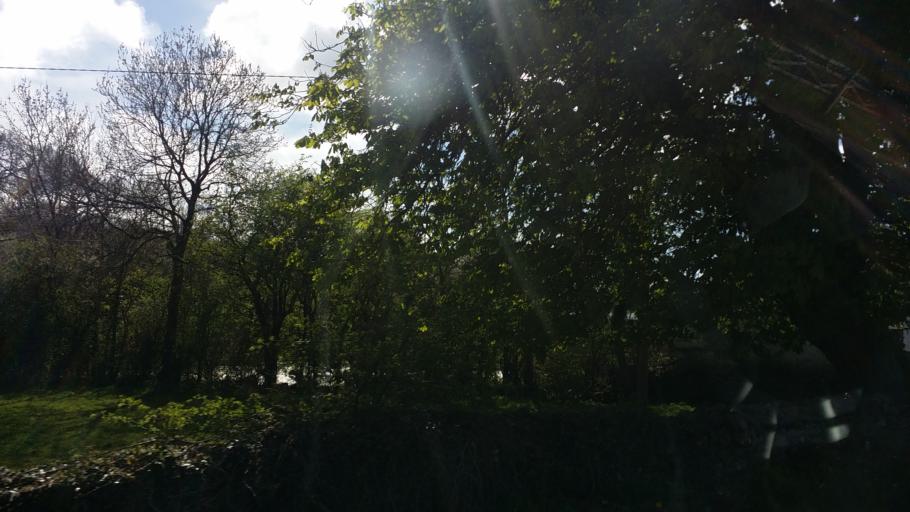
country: IE
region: Ulster
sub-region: County Donegal
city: Ballyshannon
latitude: 54.4839
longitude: -8.1221
